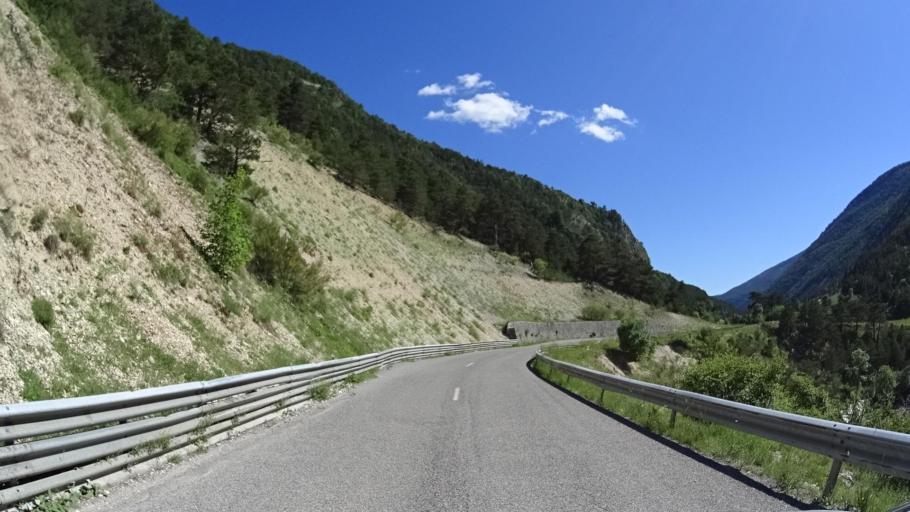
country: FR
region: Provence-Alpes-Cote d'Azur
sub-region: Departement des Alpes-de-Haute-Provence
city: Annot
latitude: 44.0577
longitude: 6.5745
